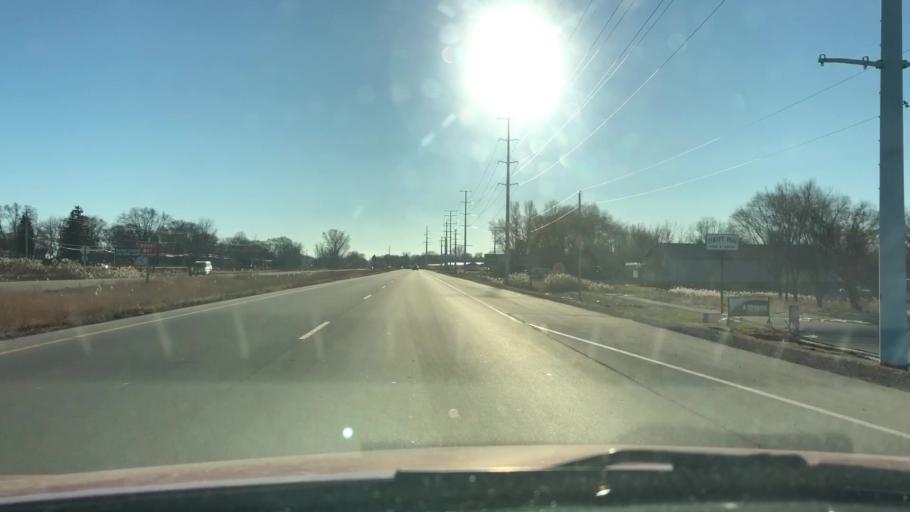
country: US
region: Wisconsin
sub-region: Brown County
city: De Pere
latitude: 44.4619
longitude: -88.0727
